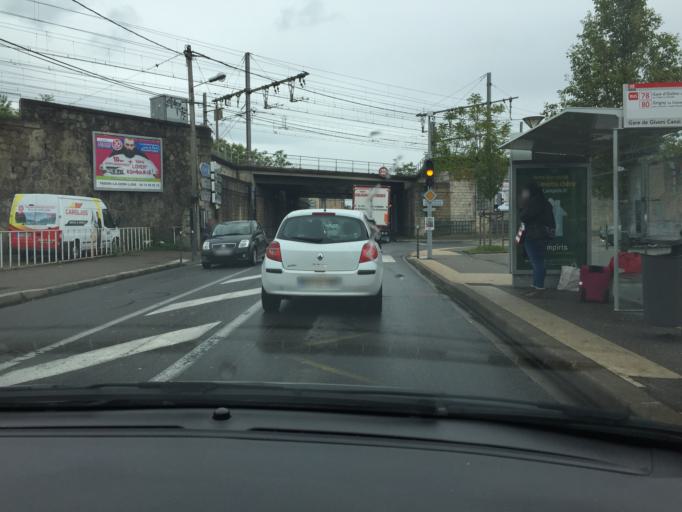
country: FR
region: Rhone-Alpes
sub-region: Departement du Rhone
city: Givors
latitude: 45.5940
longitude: 4.7700
